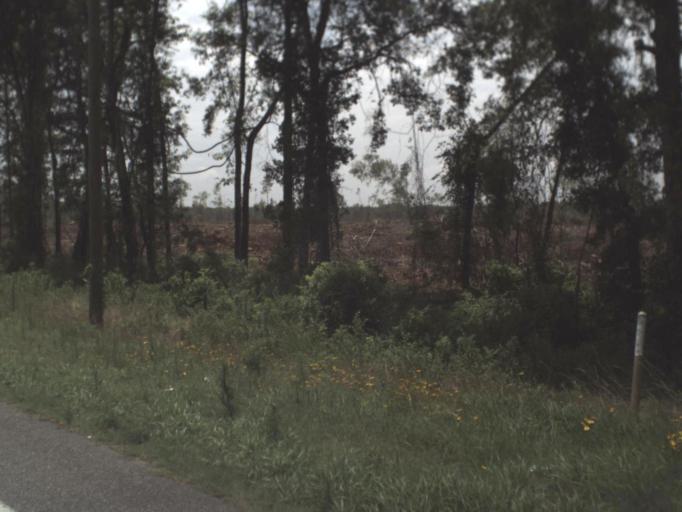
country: US
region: Florida
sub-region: Madison County
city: Madison
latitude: 30.4472
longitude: -83.3410
